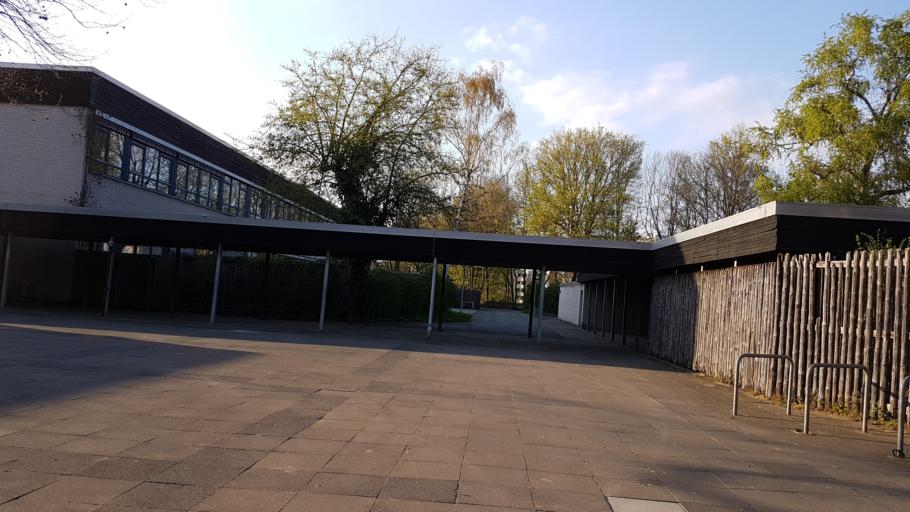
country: DE
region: Lower Saxony
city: Ronnenberg
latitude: 52.3442
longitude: 9.6836
